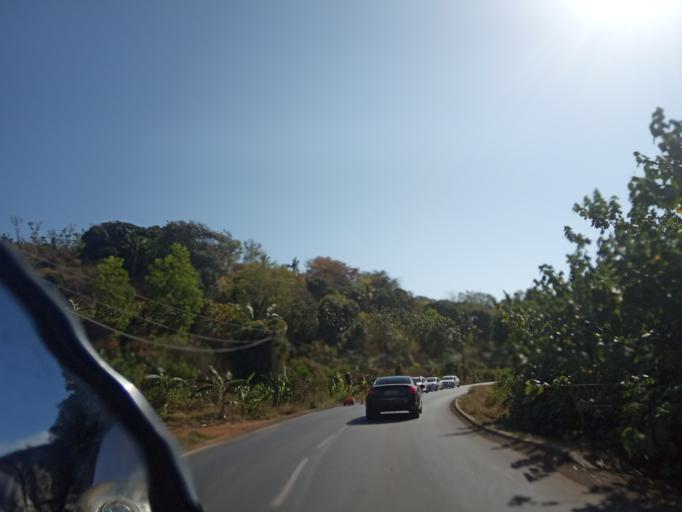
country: YT
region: Bandrele
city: Bandrele
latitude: -12.9170
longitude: 45.1855
